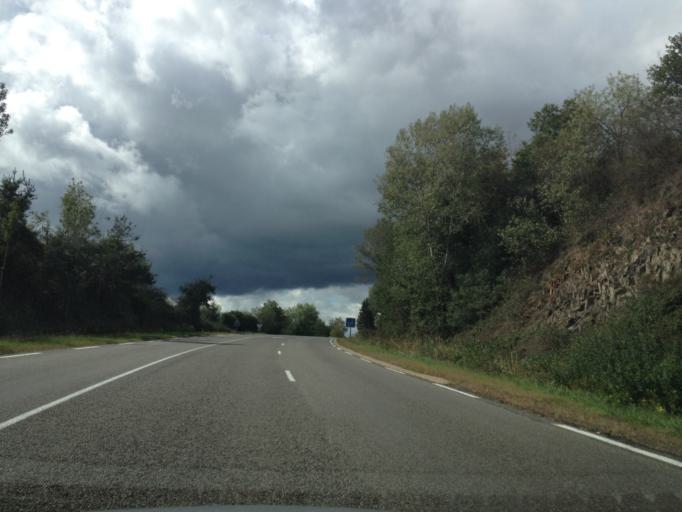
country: FR
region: Rhone-Alpes
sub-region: Departement de la Loire
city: Saint-Symphorien-de-Lay
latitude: 45.9415
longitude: 4.2542
